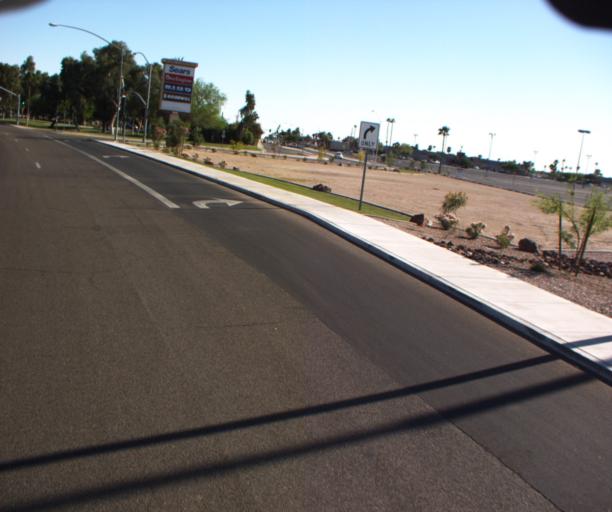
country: US
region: Arizona
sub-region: Yuma County
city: Yuma
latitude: 32.6722
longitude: -114.6244
